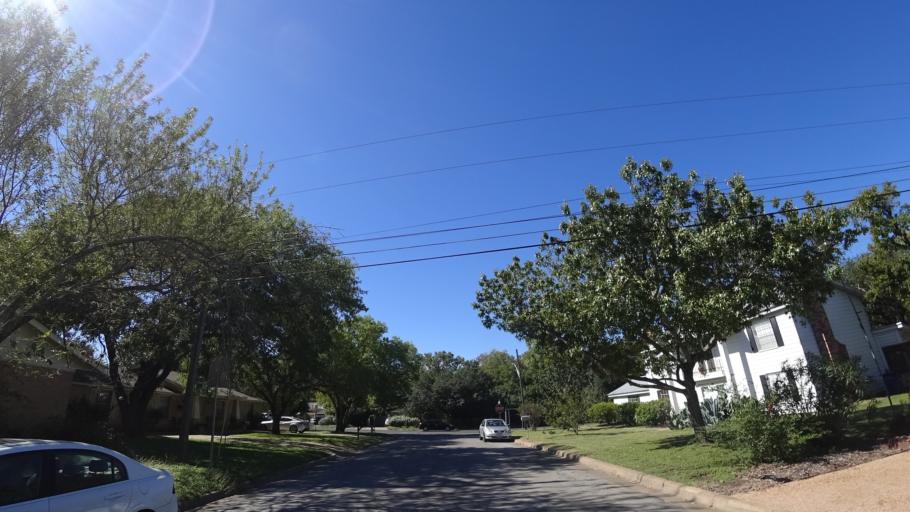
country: US
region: Texas
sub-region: Travis County
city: Austin
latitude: 30.2300
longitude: -97.7466
